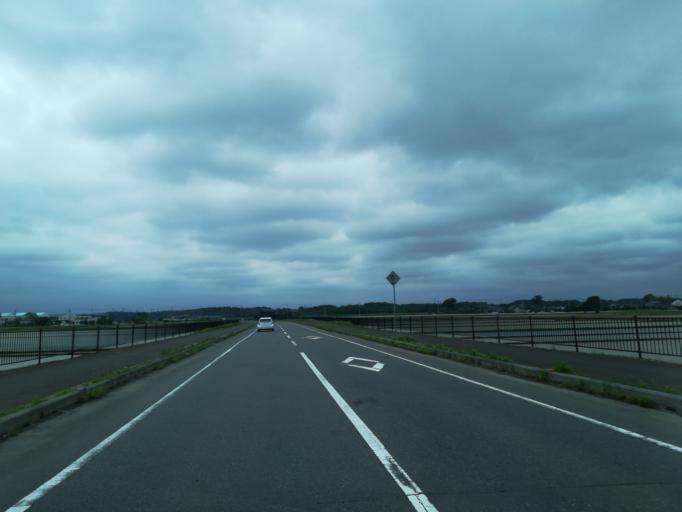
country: JP
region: Ibaraki
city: Tsukuba
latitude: 36.1297
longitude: 140.1388
